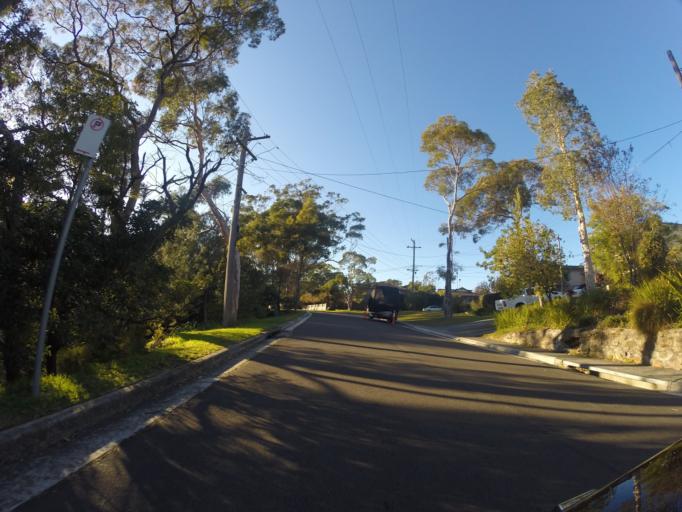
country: AU
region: New South Wales
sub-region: Sutherland Shire
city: Gymea Bay
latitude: -34.0522
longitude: 151.0911
